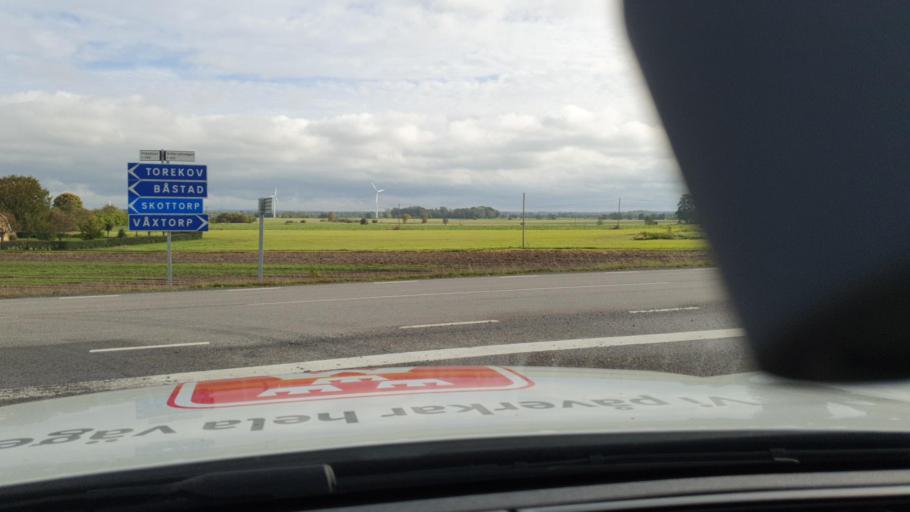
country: SE
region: Halland
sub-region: Laholms Kommun
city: Mellbystrand
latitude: 56.4232
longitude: 12.9544
